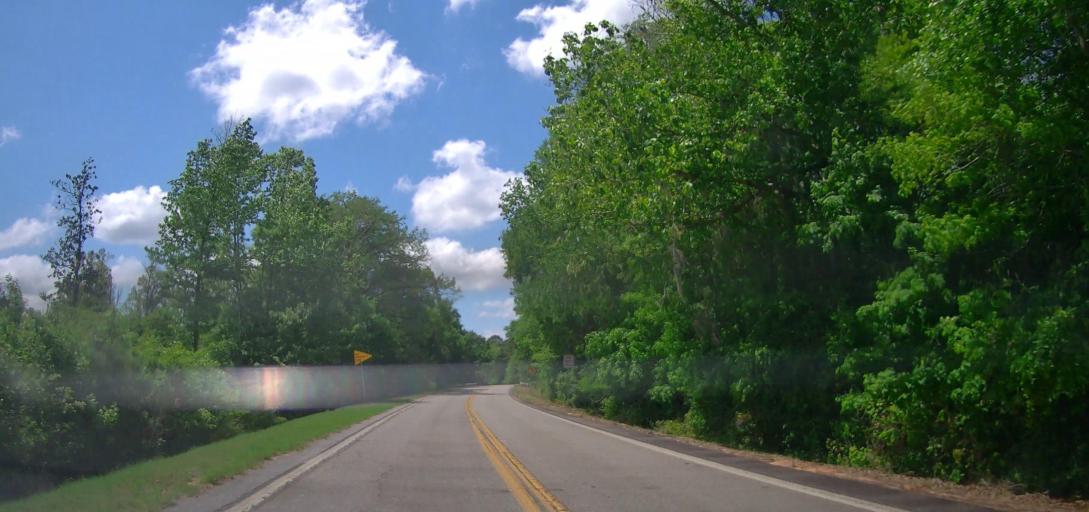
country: US
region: Georgia
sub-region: Bleckley County
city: Cochran
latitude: 32.4664
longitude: -83.2799
